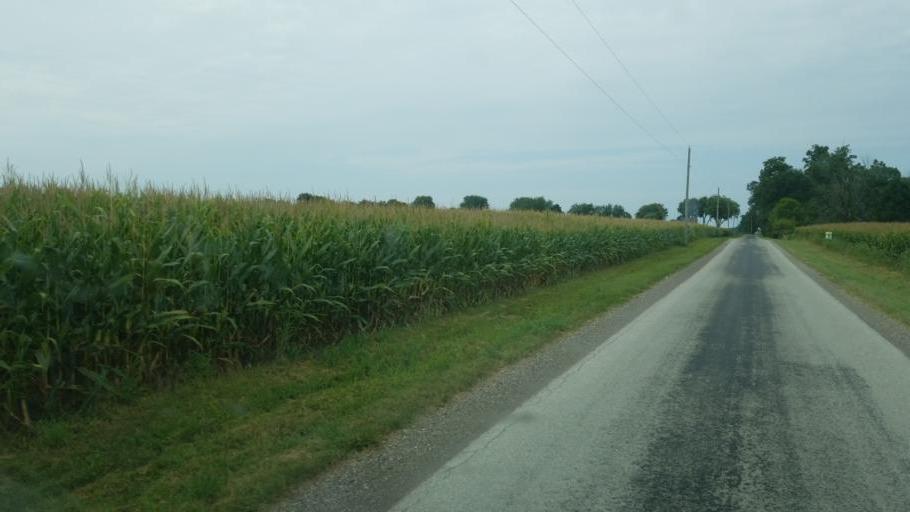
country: US
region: Ohio
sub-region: Marion County
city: Marion
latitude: 40.5129
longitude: -83.1271
